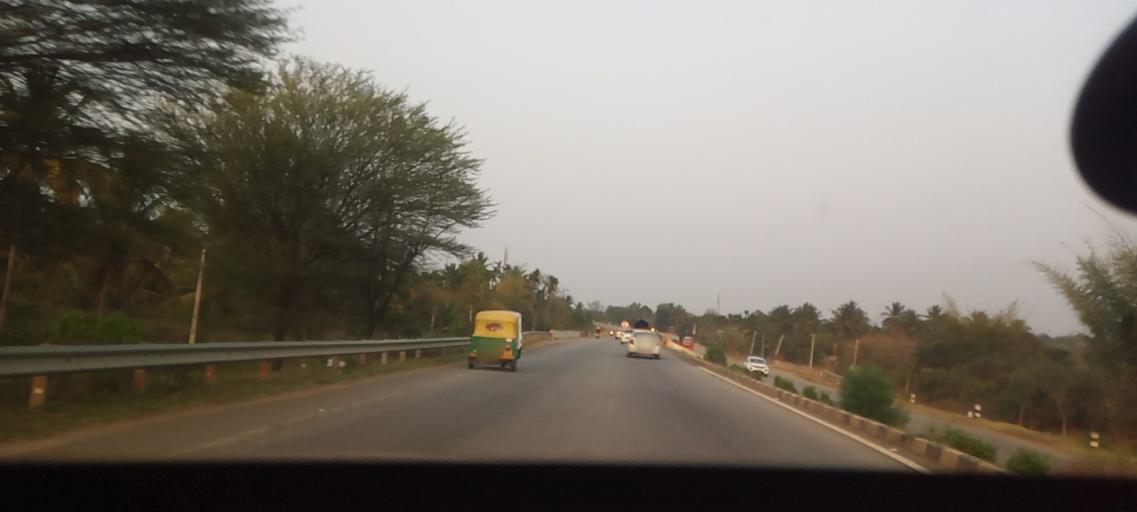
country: IN
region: Karnataka
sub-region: Tumkur
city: Kunigal
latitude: 13.0440
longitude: 77.1345
